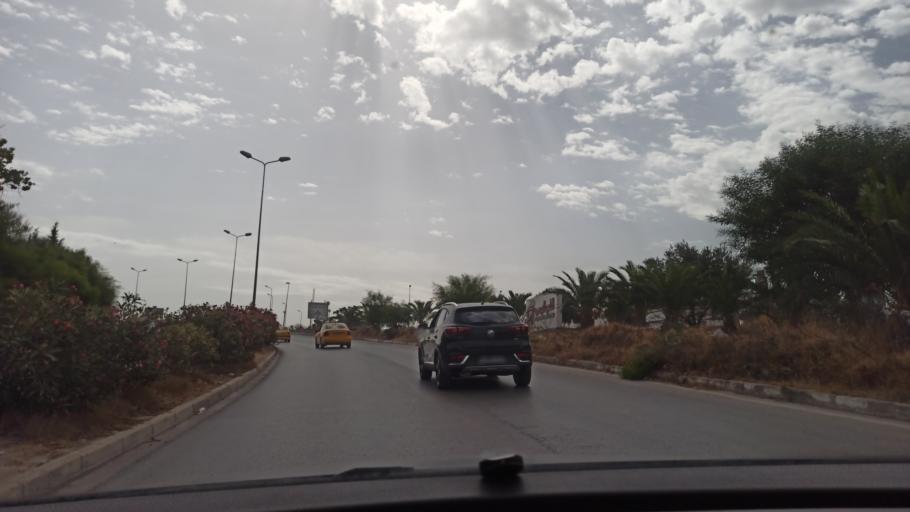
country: TN
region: Tunis
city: Tunis
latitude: 36.8298
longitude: 10.1589
